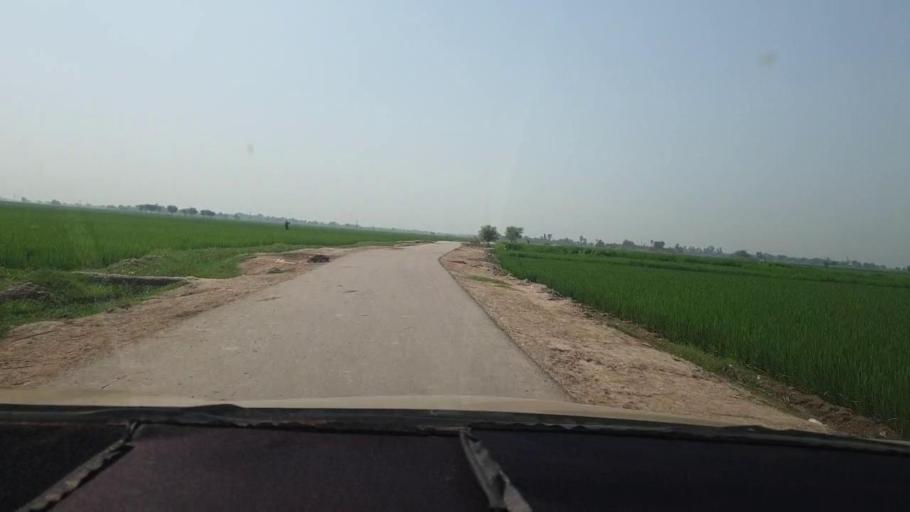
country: PK
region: Sindh
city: Kambar
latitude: 27.5676
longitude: 68.0444
